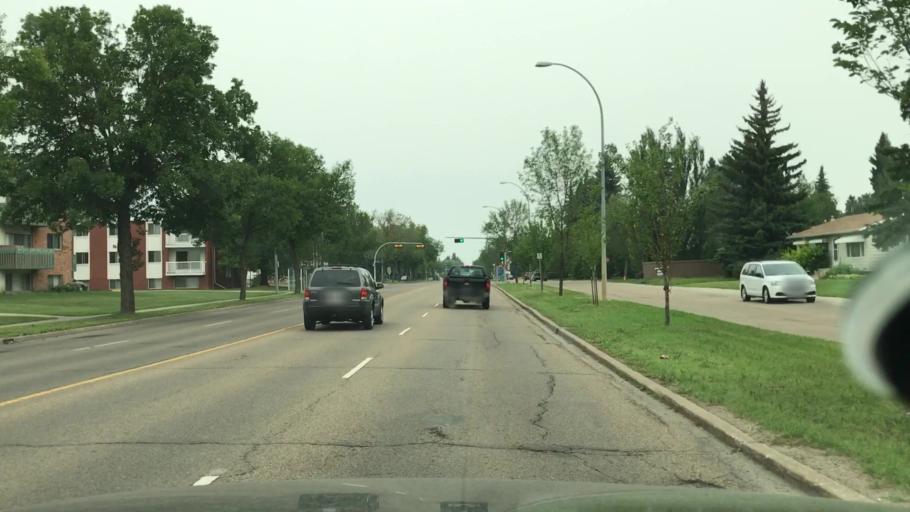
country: CA
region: Alberta
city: Edmonton
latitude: 53.5274
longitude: -113.5779
